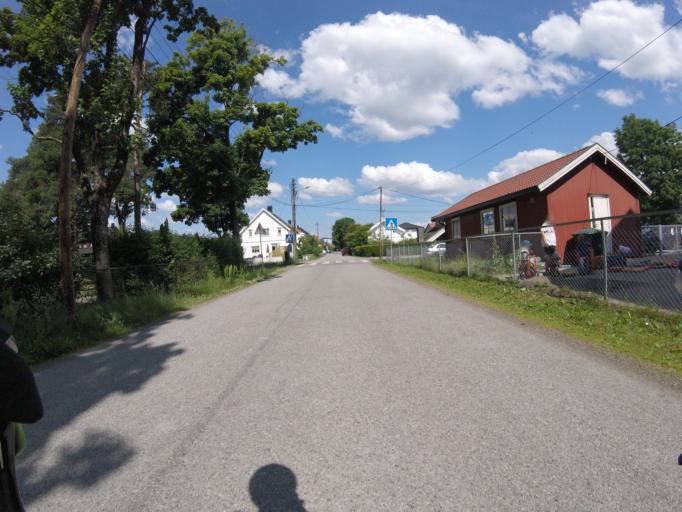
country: NO
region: Akershus
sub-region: Skedsmo
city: Lillestrom
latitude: 59.9539
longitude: 11.0627
